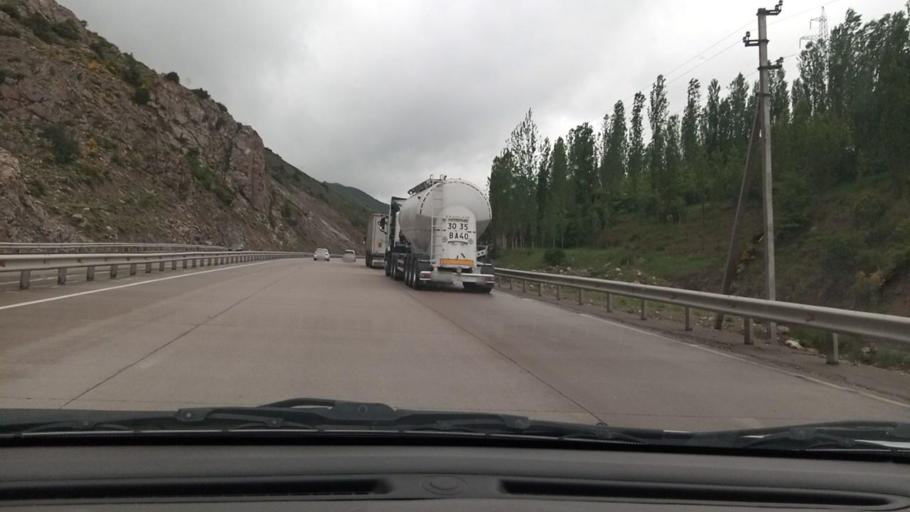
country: UZ
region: Toshkent
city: Angren
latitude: 41.0466
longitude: 70.5720
